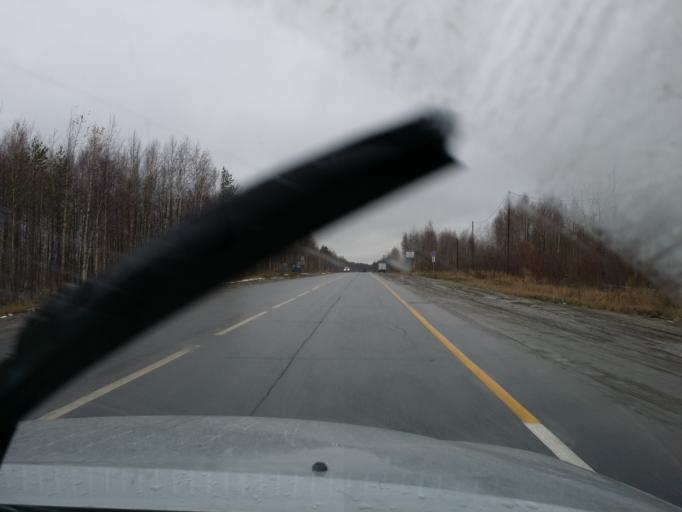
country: RU
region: Khanty-Mansiyskiy Avtonomnyy Okrug
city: Megion
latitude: 61.0900
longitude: 76.0949
